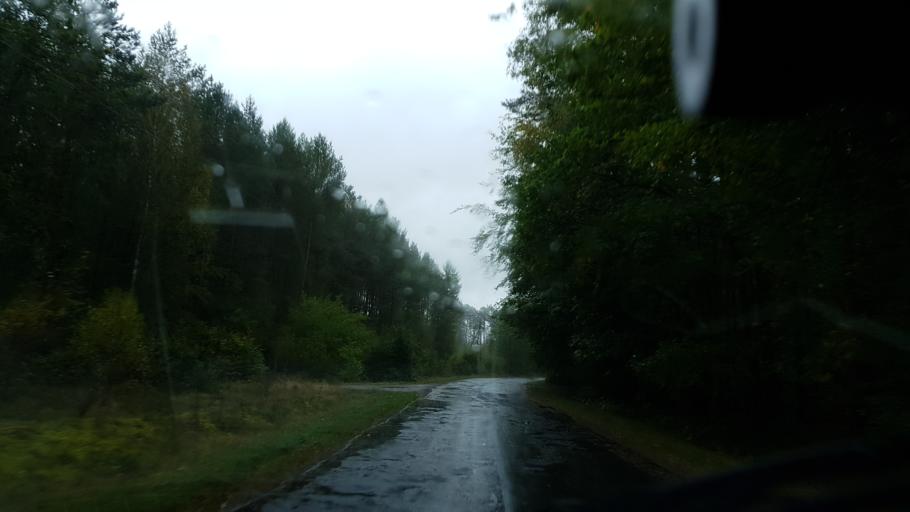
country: PL
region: West Pomeranian Voivodeship
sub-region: Powiat goleniowski
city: Przybiernow
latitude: 53.6722
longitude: 14.7326
